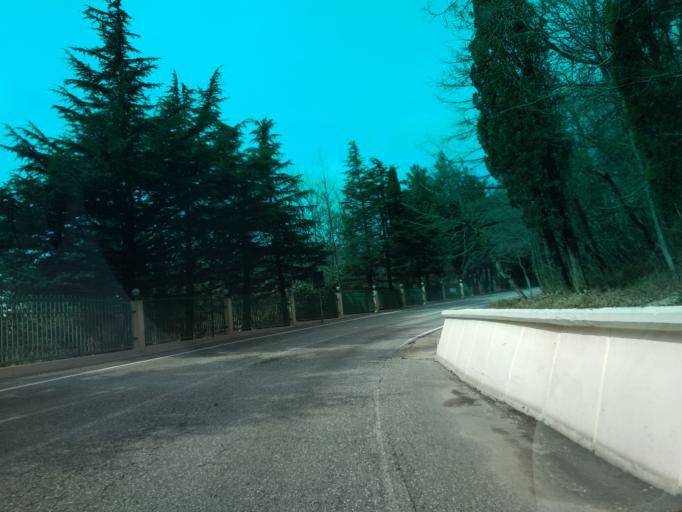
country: RU
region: Krasnodarskiy
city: Shepsi
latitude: 44.0486
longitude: 39.1313
